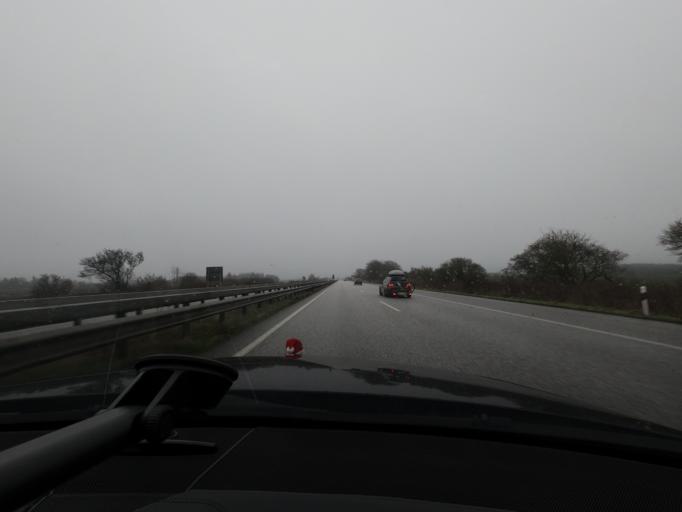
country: DE
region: Schleswig-Holstein
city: Bollingstedt
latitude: 54.6314
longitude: 9.4396
